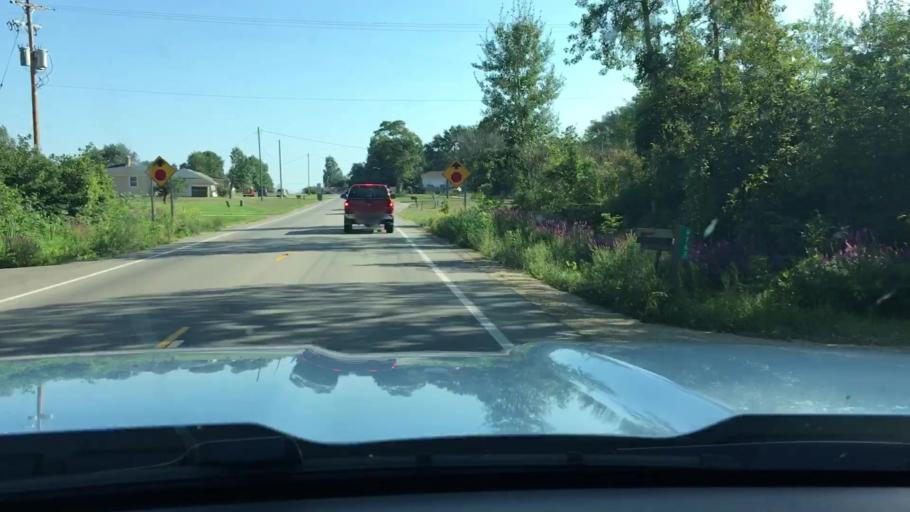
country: US
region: Michigan
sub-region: Ottawa County
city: Allendale
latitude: 42.9460
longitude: -85.9530
